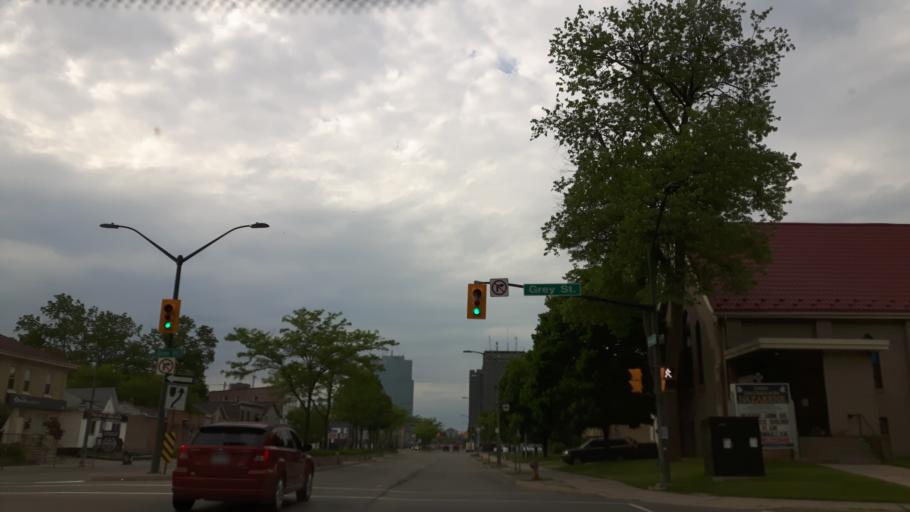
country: CA
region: Ontario
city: London
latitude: 42.9777
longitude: -81.2415
